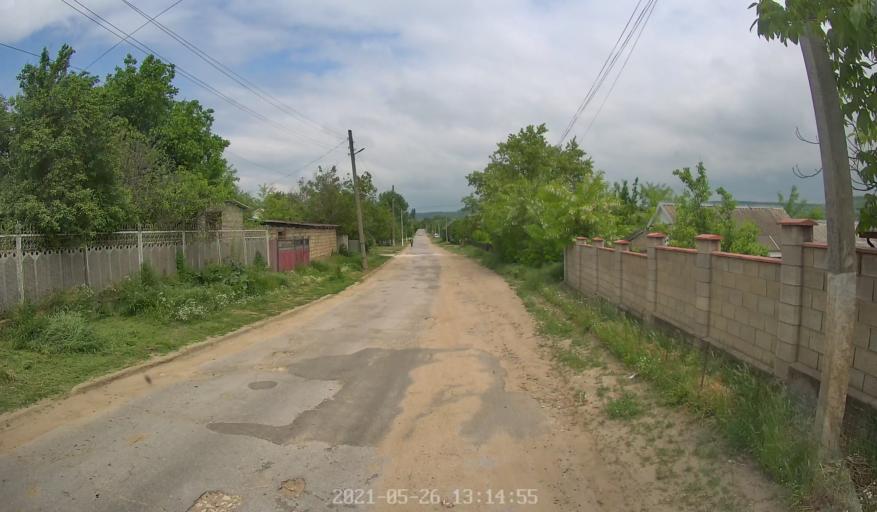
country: MD
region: Hincesti
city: Dancu
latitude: 46.7586
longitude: 28.3401
